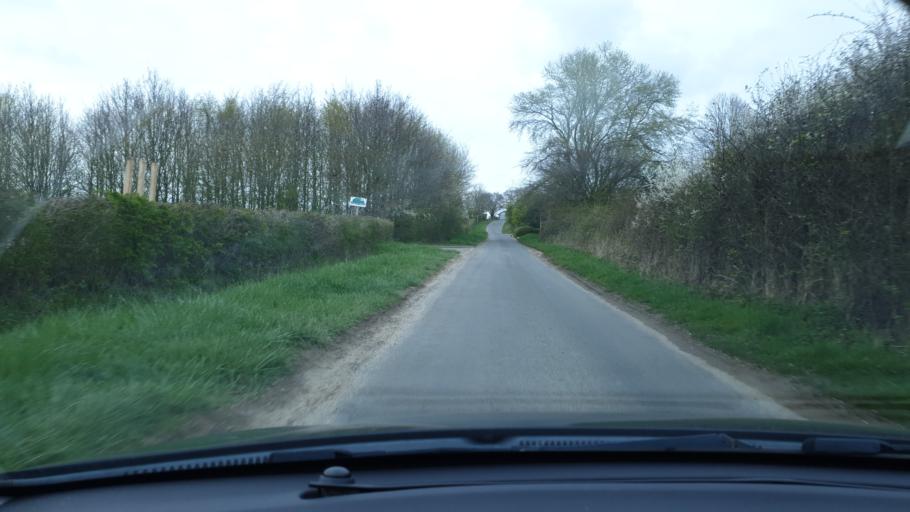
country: GB
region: England
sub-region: Essex
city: Mistley
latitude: 51.9408
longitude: 1.1567
